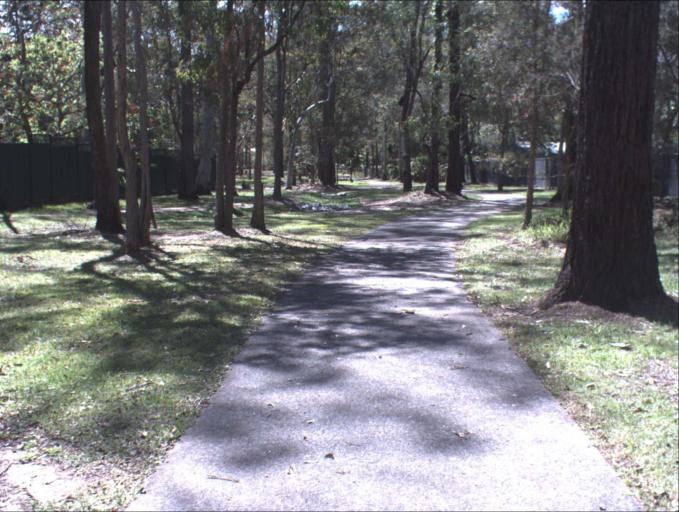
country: AU
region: Queensland
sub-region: Brisbane
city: Forest Lake
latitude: -27.6624
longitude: 153.0021
